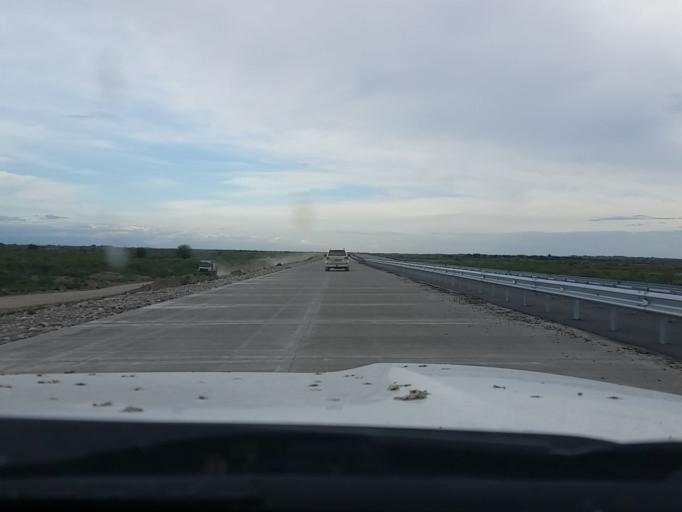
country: KZ
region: Almaty Oblysy
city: Zharkent
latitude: 44.1020
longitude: 80.0775
